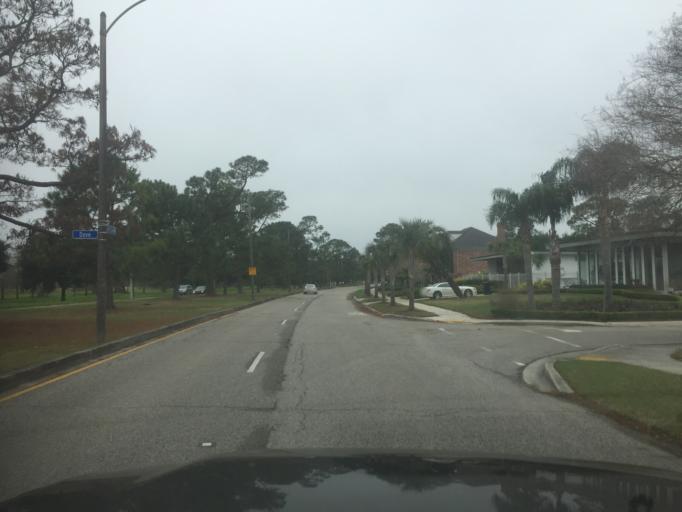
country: US
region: Louisiana
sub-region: Orleans Parish
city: New Orleans
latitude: 30.0186
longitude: -90.0919
